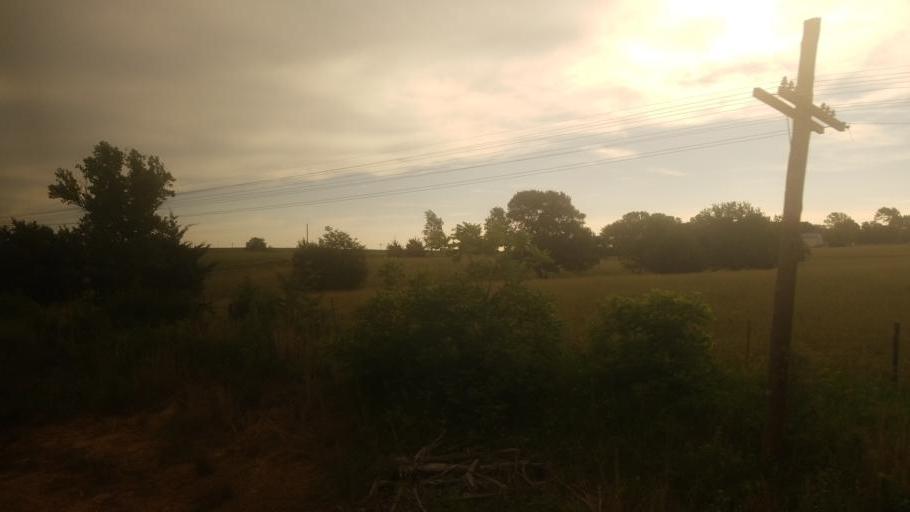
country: US
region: Kansas
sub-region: Osage County
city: Carbondale
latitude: 38.8977
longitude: -95.7001
